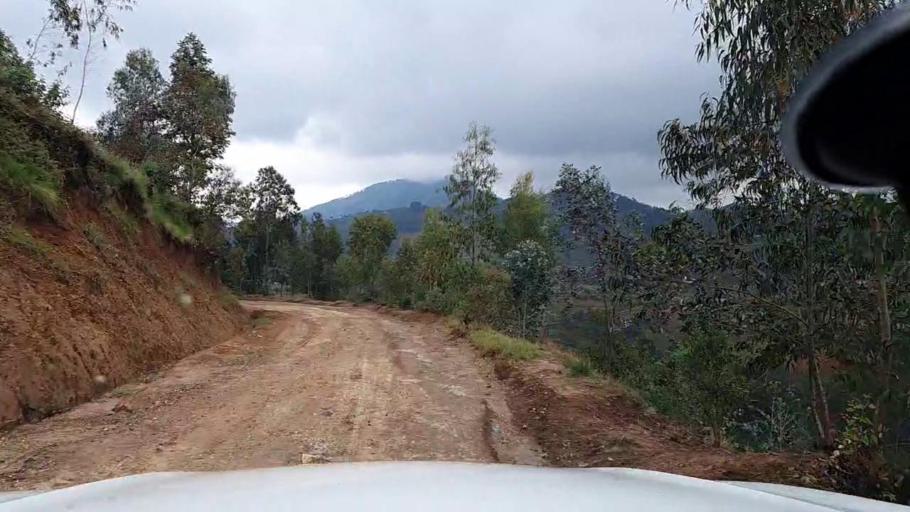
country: RW
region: Western Province
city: Kibuye
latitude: -2.0840
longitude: 29.5091
